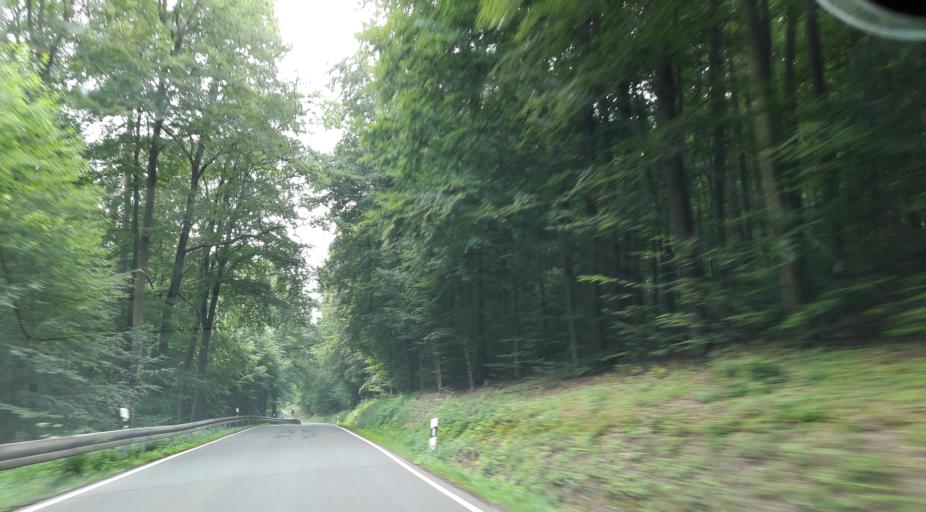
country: DE
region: Saarland
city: Hangard
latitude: 49.4018
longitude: 7.2385
